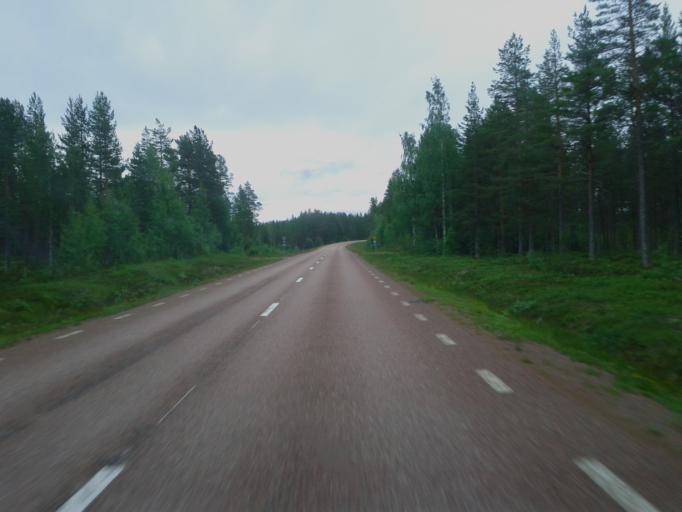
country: SE
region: Dalarna
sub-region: Alvdalens Kommun
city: AElvdalen
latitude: 61.5264
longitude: 13.3598
